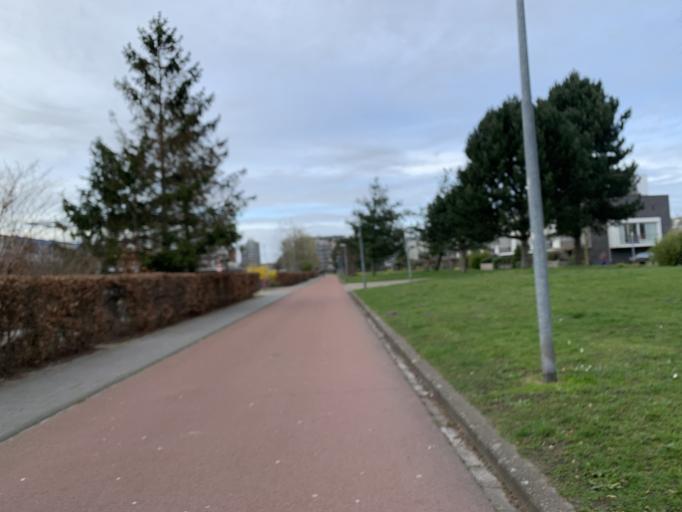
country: NL
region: Groningen
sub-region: Gemeente Groningen
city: Oosterpark
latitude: 53.2120
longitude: 6.5821
